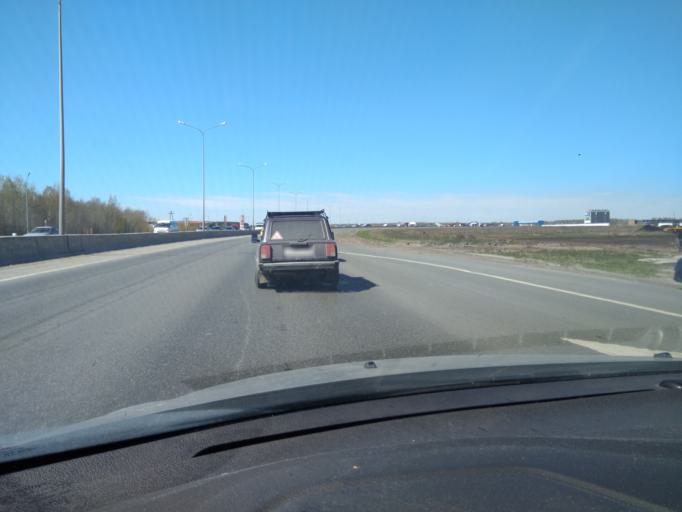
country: RU
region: Tjumen
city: Moskovskiy
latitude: 57.1342
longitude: 65.4648
